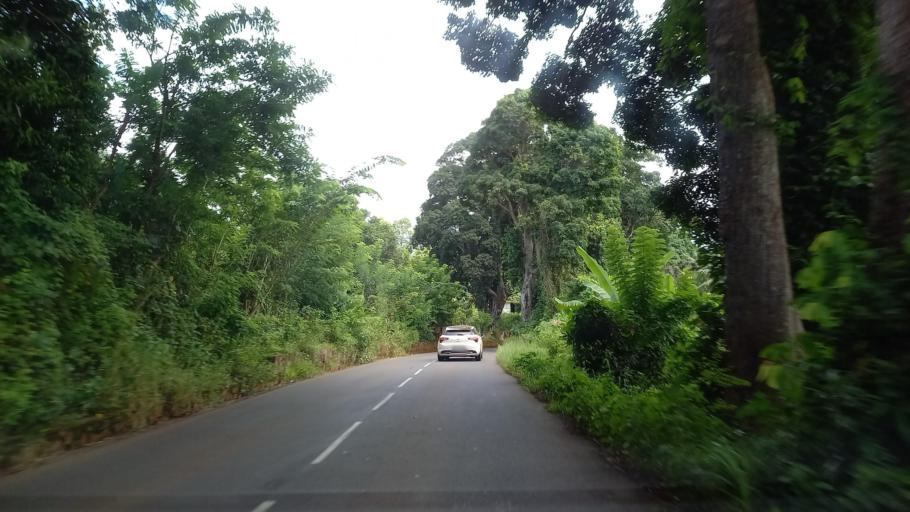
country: YT
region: Mamoudzou
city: Mamoudzou
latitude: -12.7928
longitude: 45.1858
